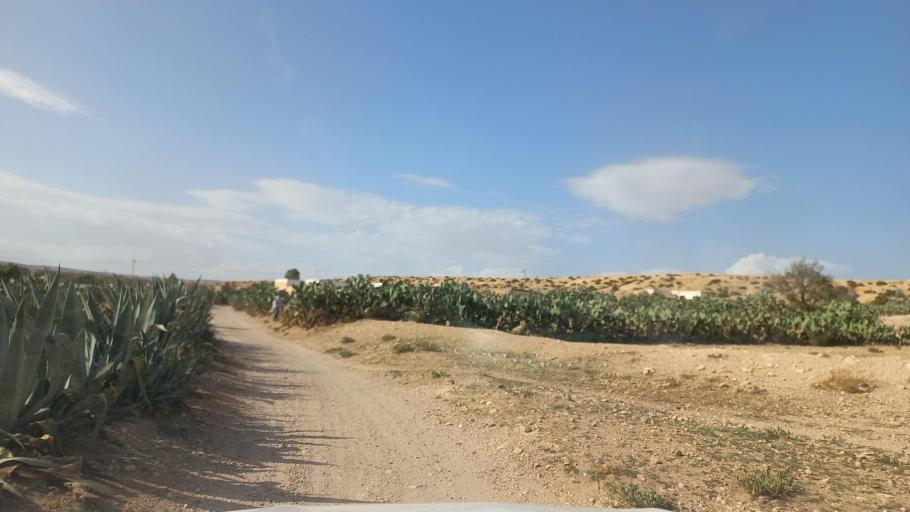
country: TN
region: Al Qasrayn
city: Kasserine
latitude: 35.2562
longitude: 8.9303
